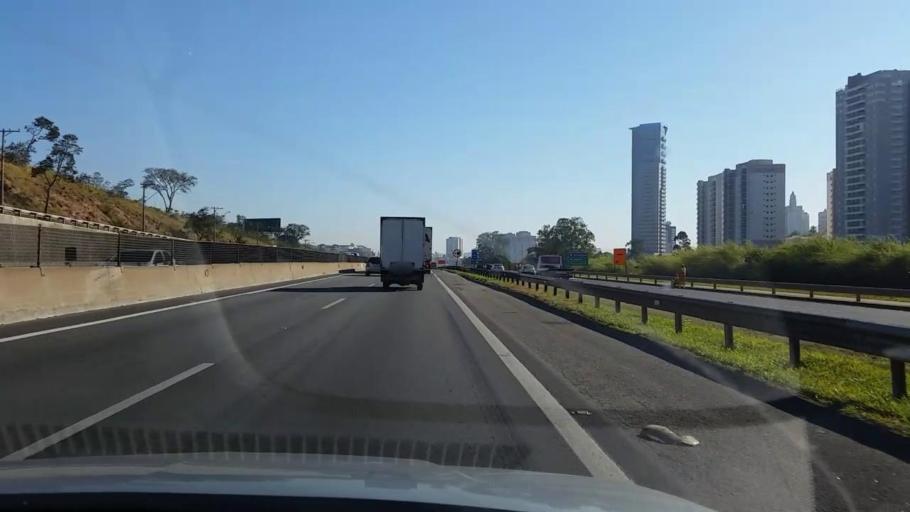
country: BR
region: Sao Paulo
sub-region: Jundiai
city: Jundiai
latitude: -23.1979
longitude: -46.9034
